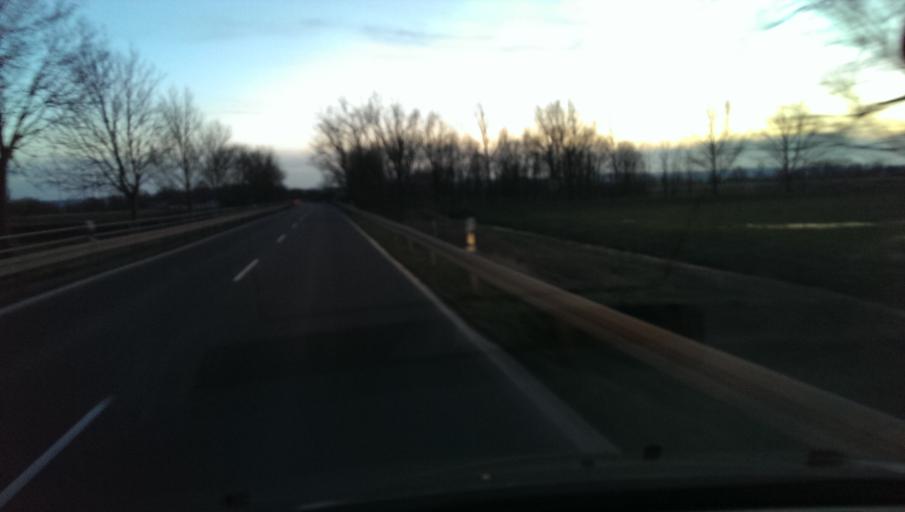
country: DE
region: Saxony-Anhalt
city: Ausleben
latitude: 52.0352
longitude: 11.0948
